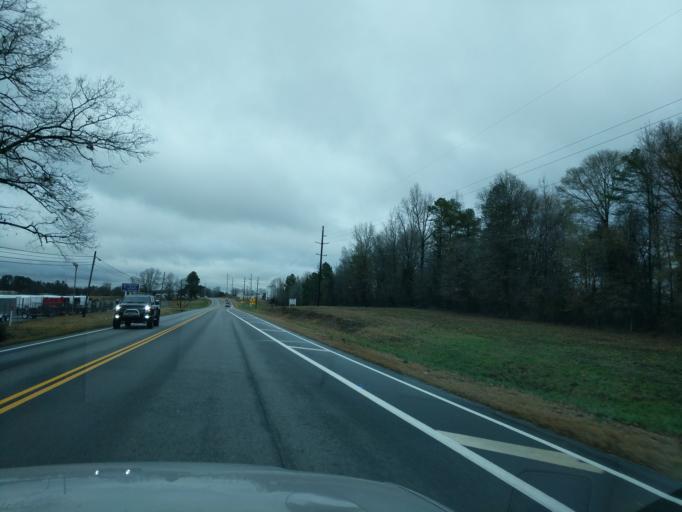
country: US
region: Georgia
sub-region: Franklin County
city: Lavonia
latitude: 34.4087
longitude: -83.1001
